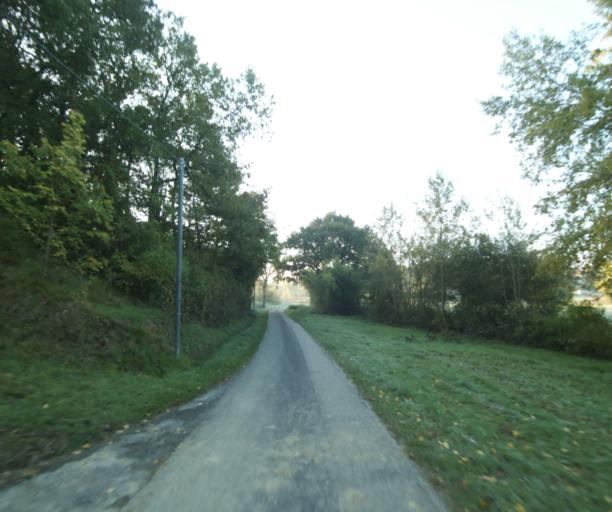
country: FR
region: Midi-Pyrenees
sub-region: Departement du Gers
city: Eauze
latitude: 43.7674
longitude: 0.1687
